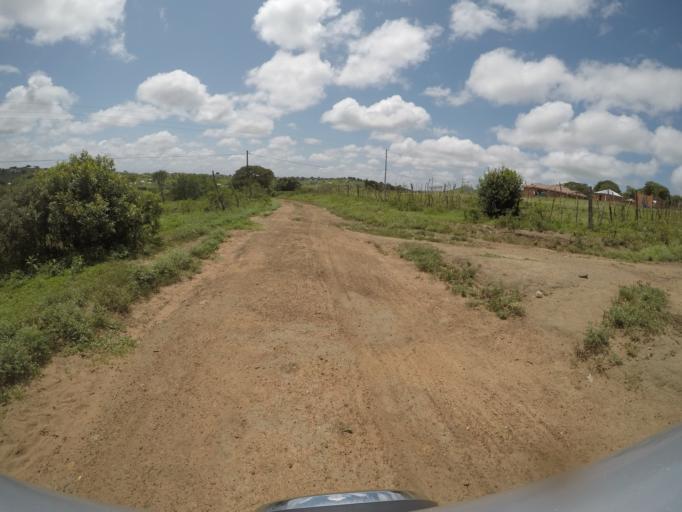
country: ZA
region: KwaZulu-Natal
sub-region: uThungulu District Municipality
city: Empangeni
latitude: -28.5837
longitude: 31.8345
